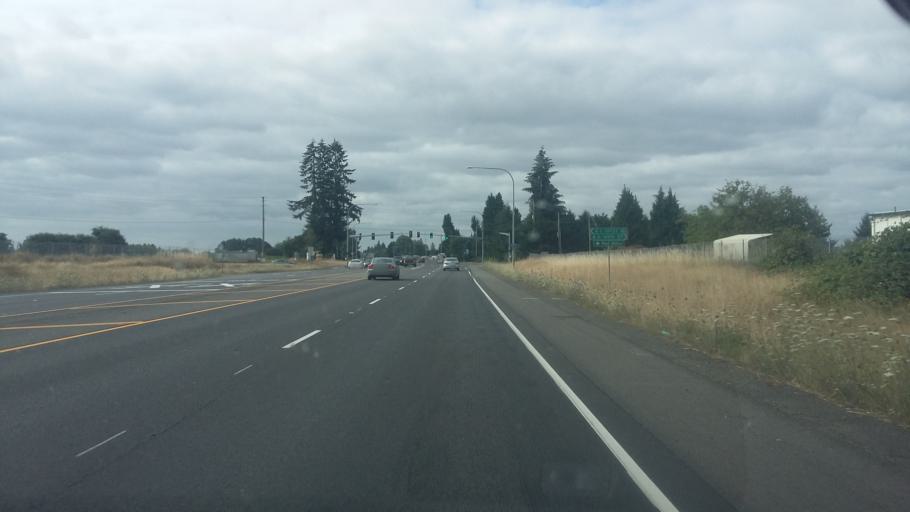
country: US
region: Washington
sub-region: Clark County
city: Brush Prairie
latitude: 45.7314
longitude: -122.5521
